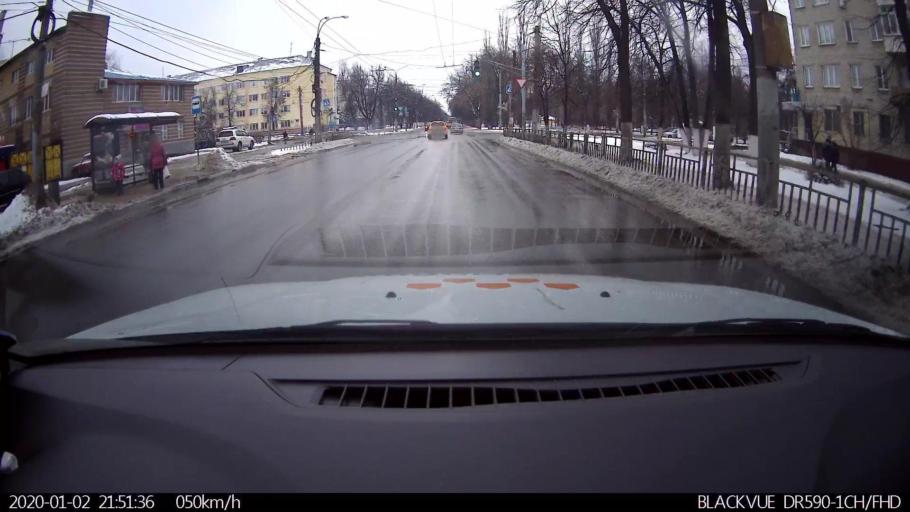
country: RU
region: Nizjnij Novgorod
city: Gorbatovka
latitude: 56.2447
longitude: 43.8651
